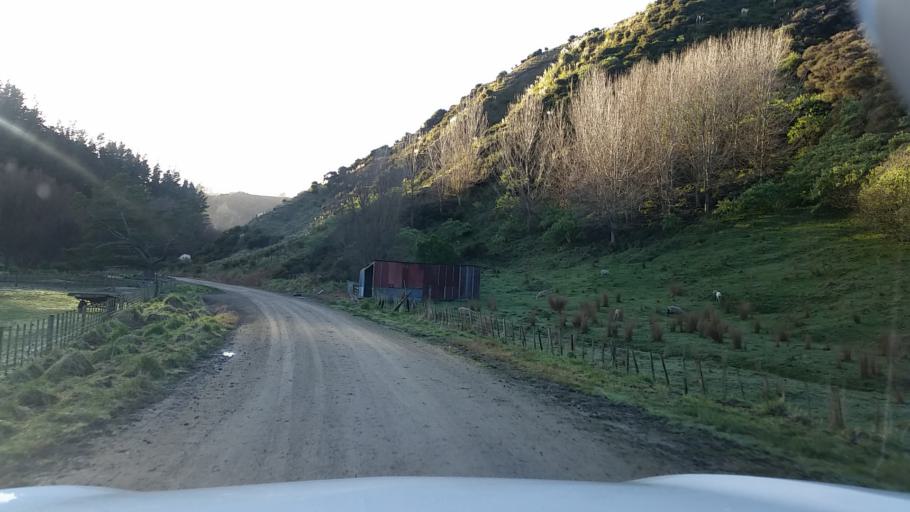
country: NZ
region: Taranaki
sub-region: South Taranaki District
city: Patea
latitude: -39.7601
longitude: 174.7288
